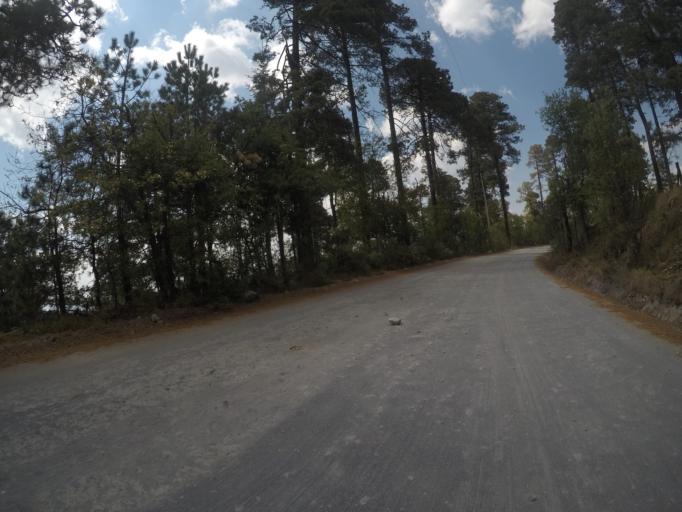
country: MX
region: Mexico
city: Cerro La Calera
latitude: 19.1457
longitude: -99.8042
